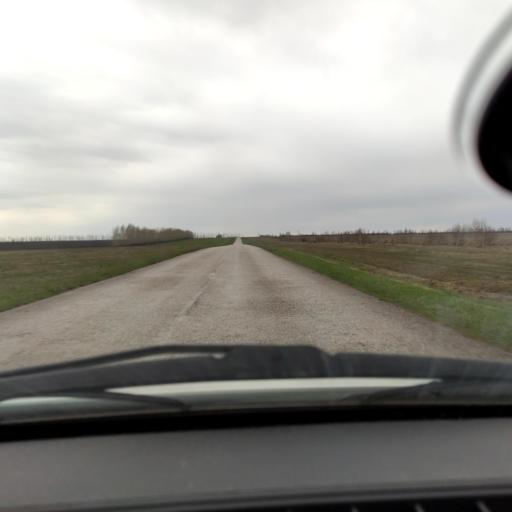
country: RU
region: Bashkortostan
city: Tolbazy
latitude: 54.1707
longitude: 55.9166
